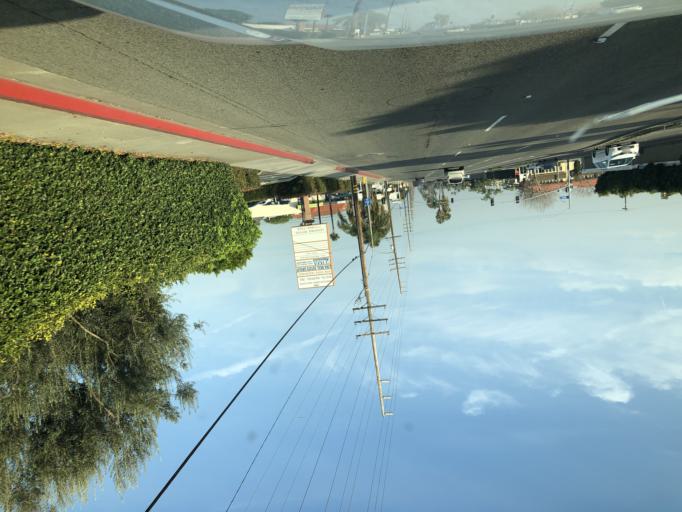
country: US
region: California
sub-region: Orange County
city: Costa Mesa
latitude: 33.6567
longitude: -117.9535
